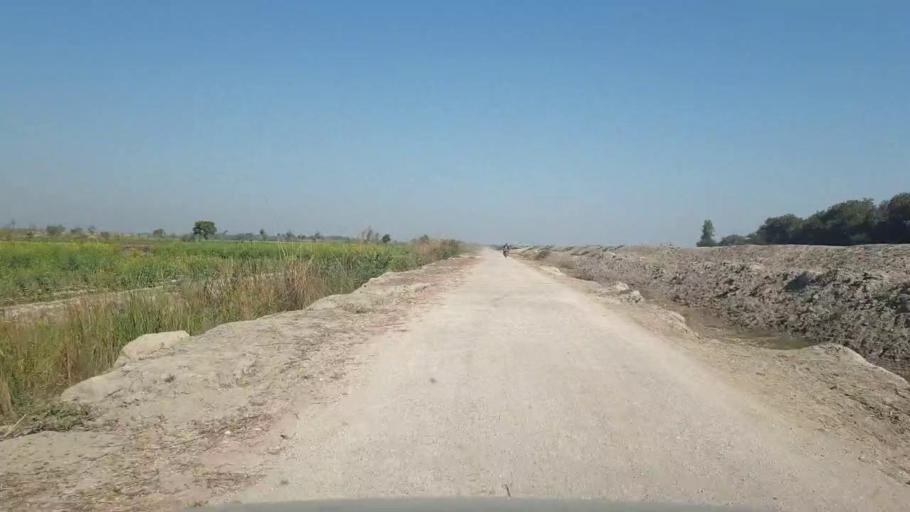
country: PK
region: Sindh
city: Mirwah Gorchani
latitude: 25.3331
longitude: 69.1020
